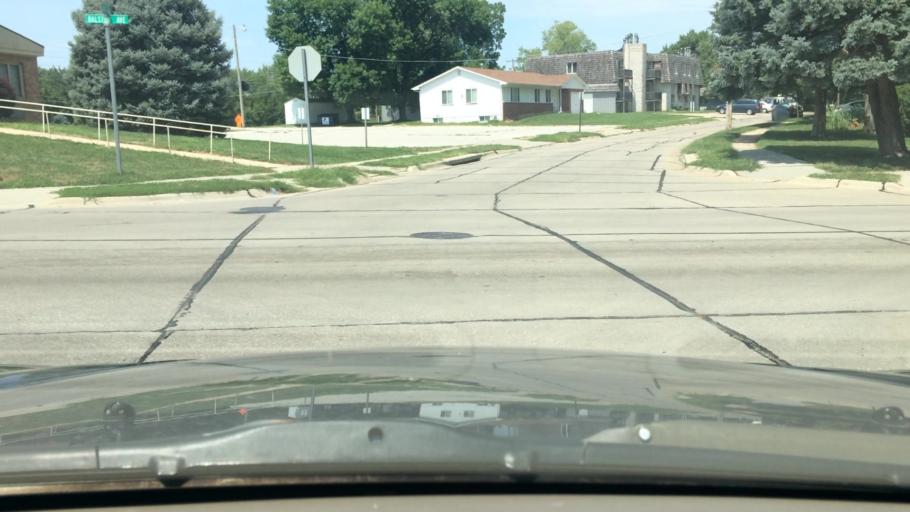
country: US
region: Nebraska
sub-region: Douglas County
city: Ralston
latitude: 41.1928
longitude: -96.0419
